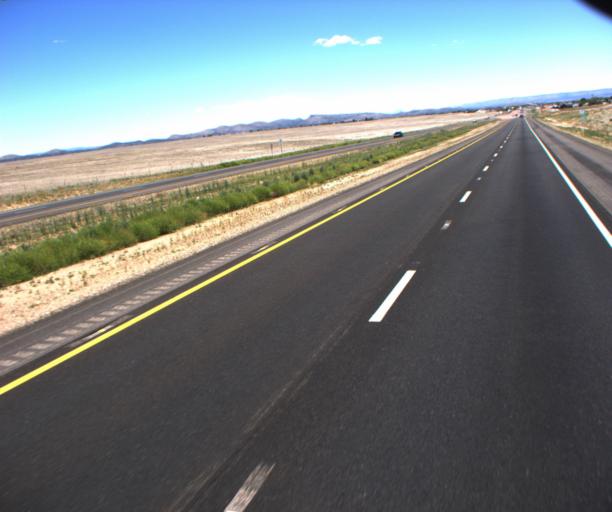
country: US
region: Arizona
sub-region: Yavapai County
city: Chino Valley
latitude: 34.6988
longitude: -112.4485
